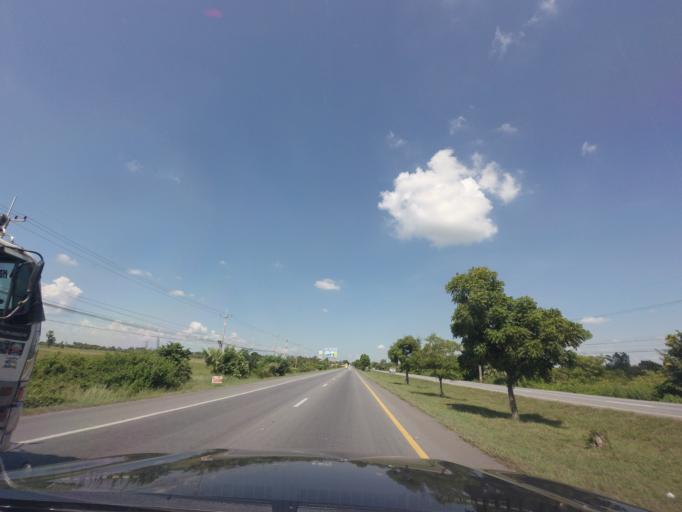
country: TH
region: Nakhon Ratchasima
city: Non Sung
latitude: 15.1403
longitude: 102.3145
